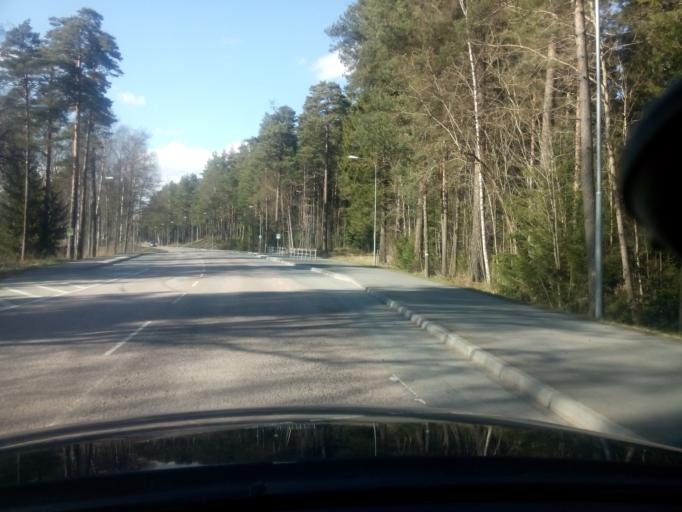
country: SE
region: Soedermanland
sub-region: Flens Kommun
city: Malmkoping
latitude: 59.1421
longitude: 16.7180
